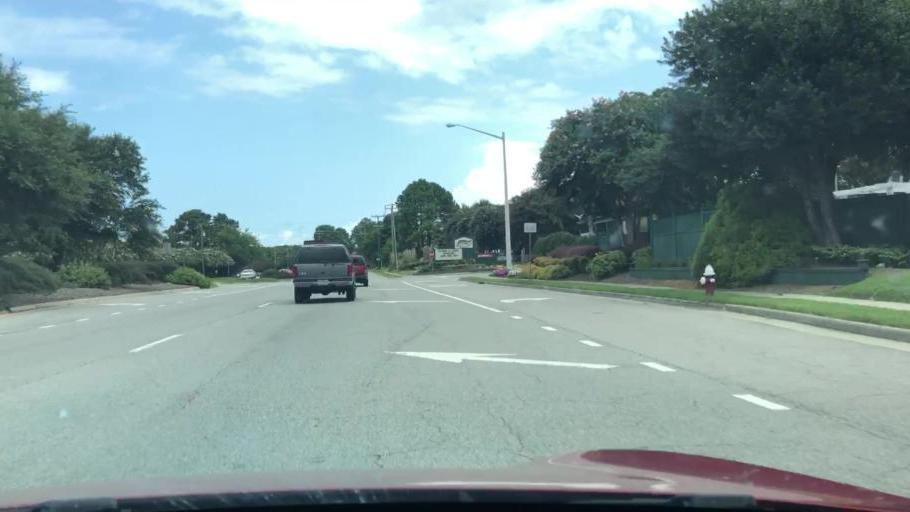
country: US
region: Virginia
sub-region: City of Chesapeake
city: Chesapeake
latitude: 36.8770
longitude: -76.1337
